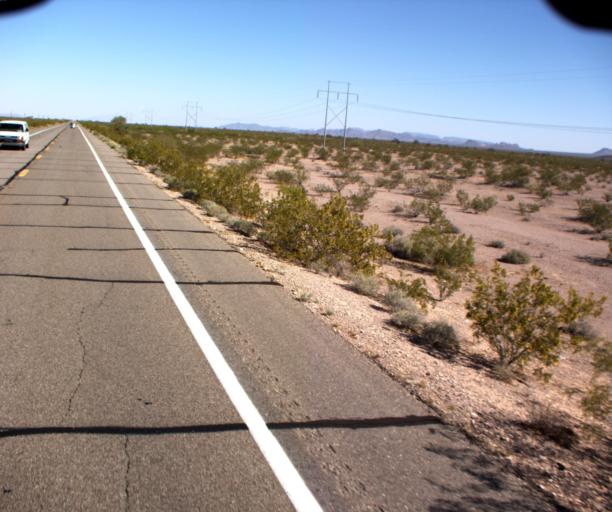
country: US
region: Arizona
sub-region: La Paz County
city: Quartzsite
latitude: 33.3259
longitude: -114.2169
